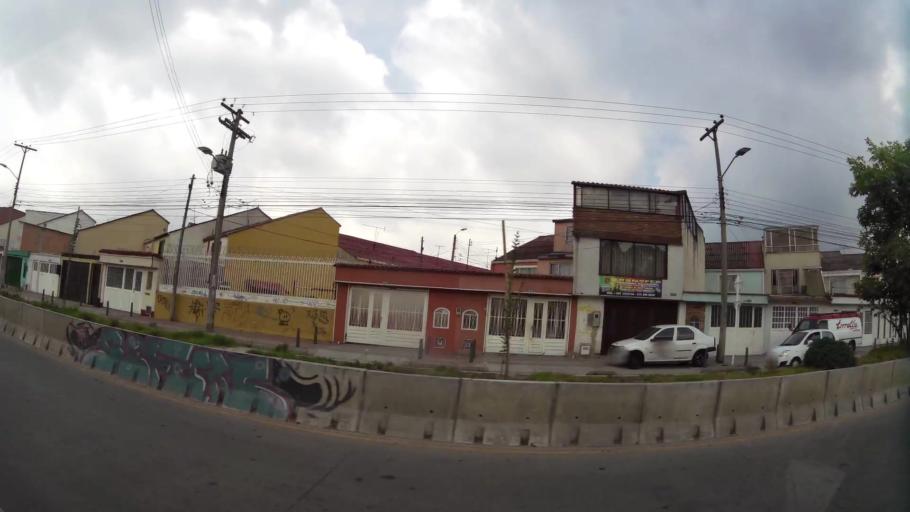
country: CO
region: Bogota D.C.
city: Bogota
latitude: 4.5890
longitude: -74.1284
